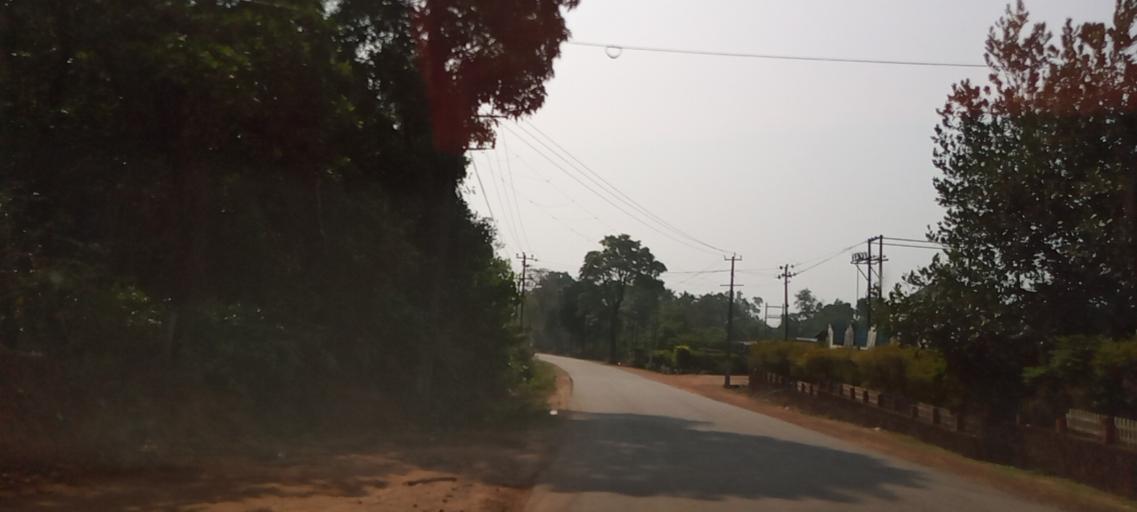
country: IN
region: Karnataka
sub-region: Udupi
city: Someshwar
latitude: 13.5240
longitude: 74.9276
